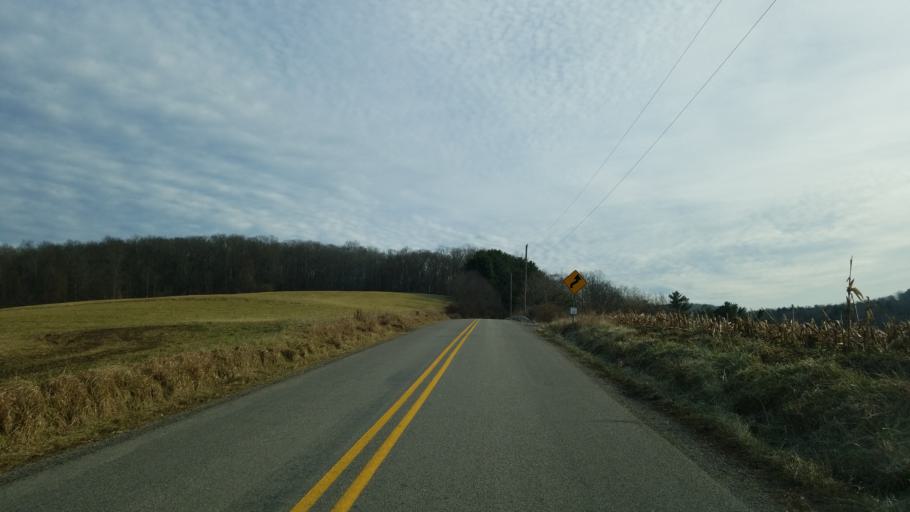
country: US
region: Pennsylvania
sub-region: Jefferson County
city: Albion
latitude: 40.9510
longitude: -78.9159
